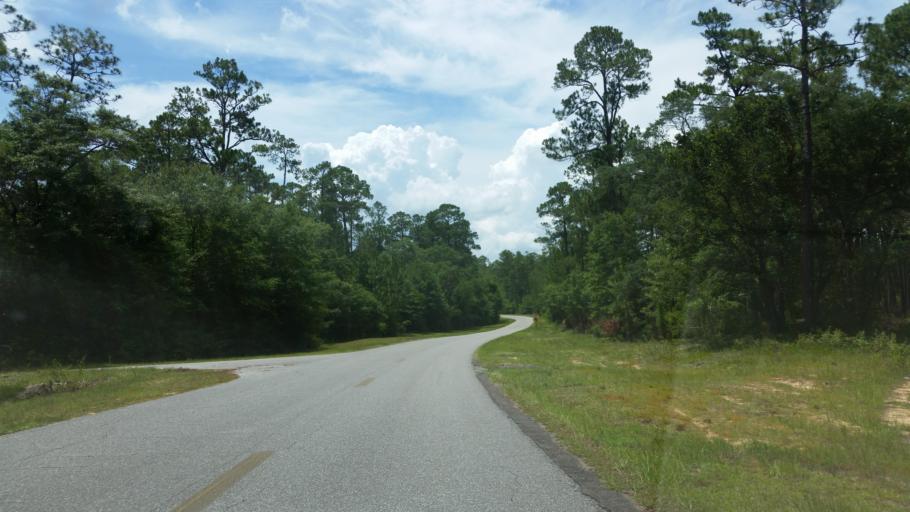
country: US
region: Florida
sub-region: Okaloosa County
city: Crestview
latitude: 30.7207
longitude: -86.7857
